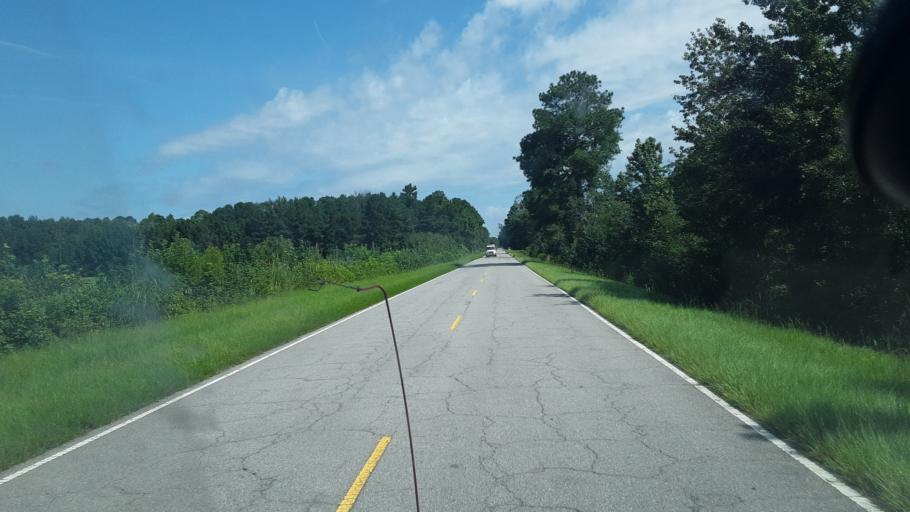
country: US
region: South Carolina
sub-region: Hampton County
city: Hampton
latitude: 33.0500
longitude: -81.0317
